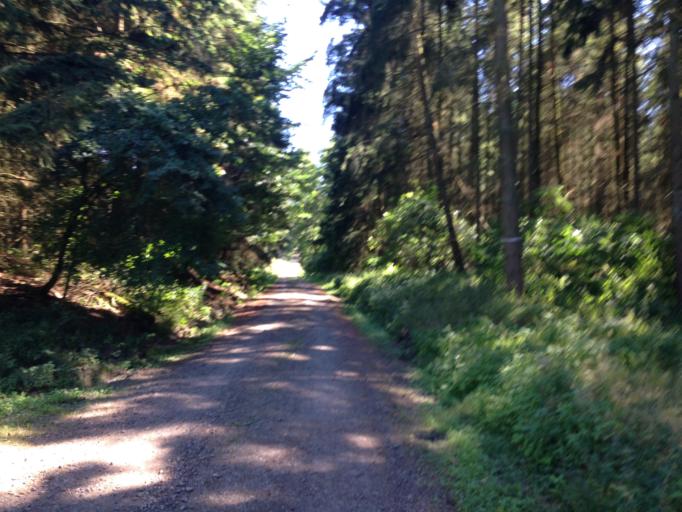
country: DE
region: Hesse
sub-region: Regierungsbezirk Giessen
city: Grossen Buseck
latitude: 50.5745
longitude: 8.7875
